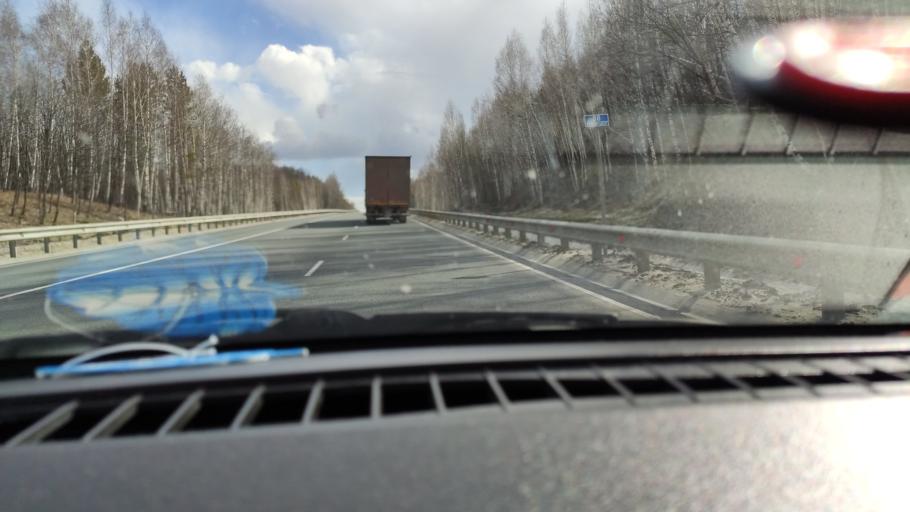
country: RU
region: Saratov
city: Khvalynsk
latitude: 52.4978
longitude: 48.0146
